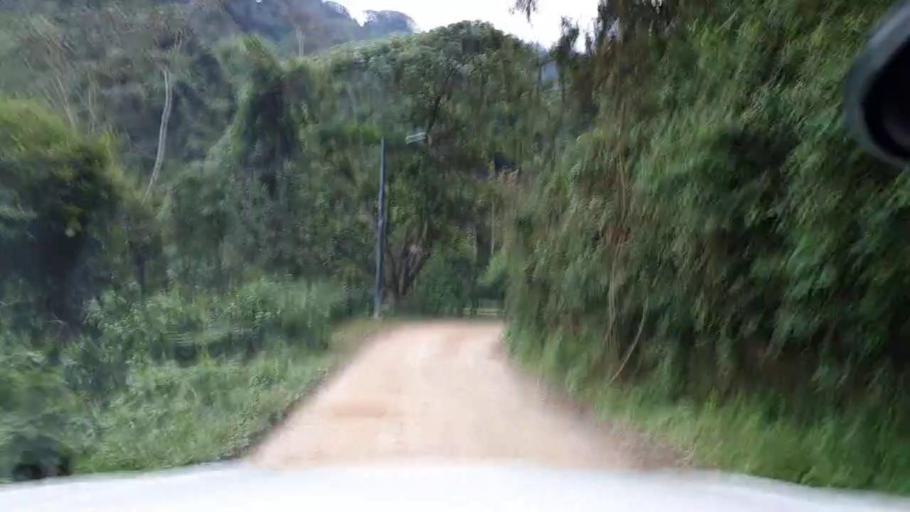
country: RW
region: Western Province
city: Cyangugu
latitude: -2.5657
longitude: 29.2313
